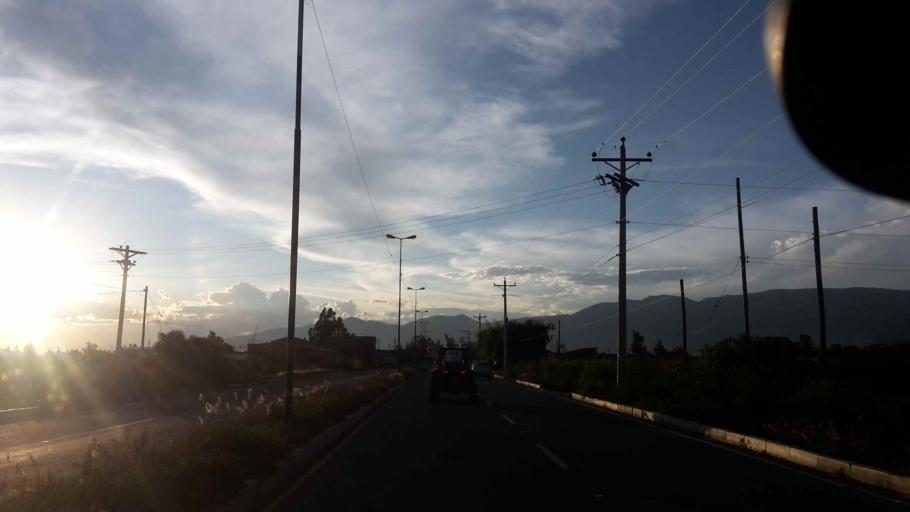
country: BO
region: Cochabamba
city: Punata
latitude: -17.5538
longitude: -65.8156
